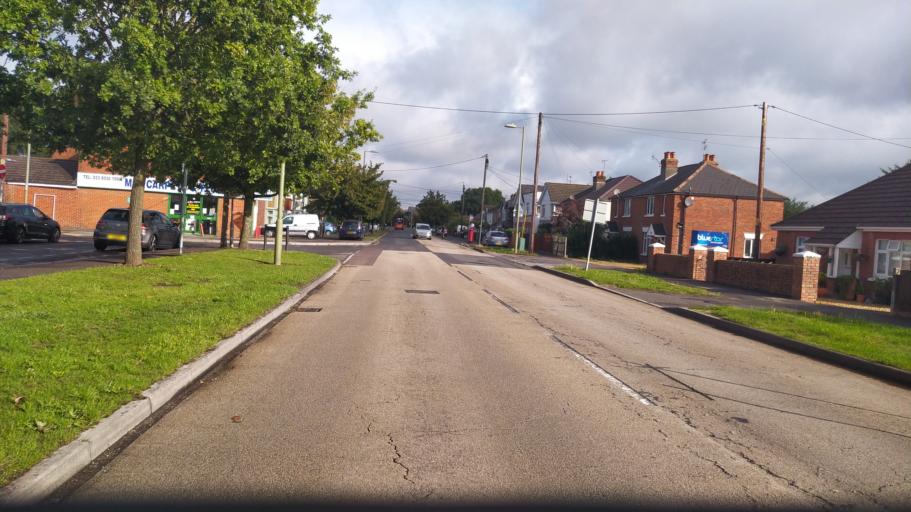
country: GB
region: England
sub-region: Hampshire
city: Totton
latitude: 50.9267
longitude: -1.5001
